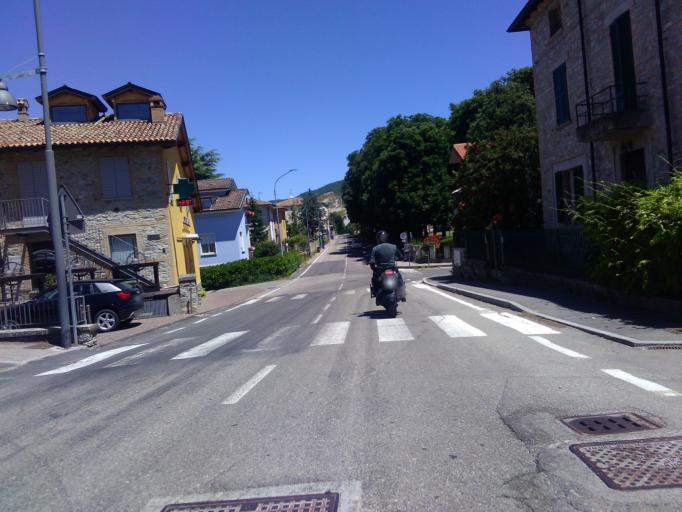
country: IT
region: Emilia-Romagna
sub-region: Provincia di Parma
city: Calestano
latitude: 44.6014
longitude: 10.1223
